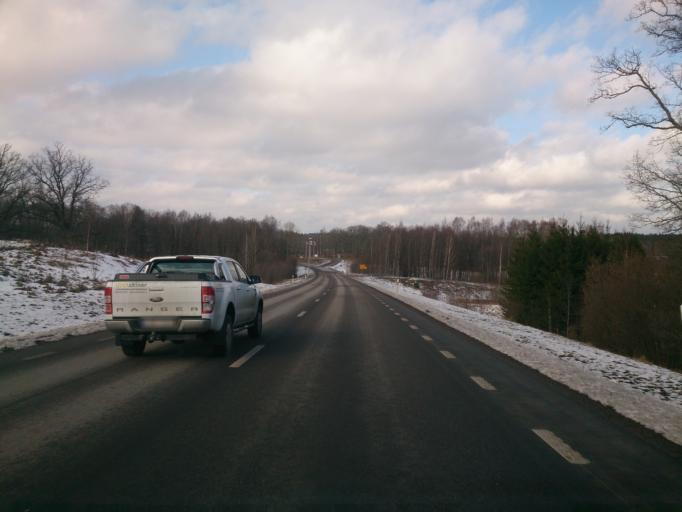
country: SE
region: OEstergoetland
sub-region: Atvidabergs Kommun
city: Atvidaberg
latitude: 58.1919
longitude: 16.0224
